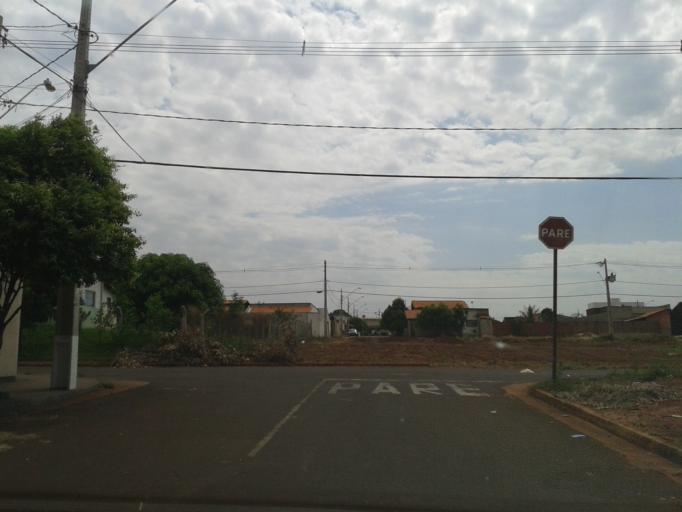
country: BR
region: Minas Gerais
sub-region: Ituiutaba
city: Ituiutaba
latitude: -18.9830
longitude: -49.4382
